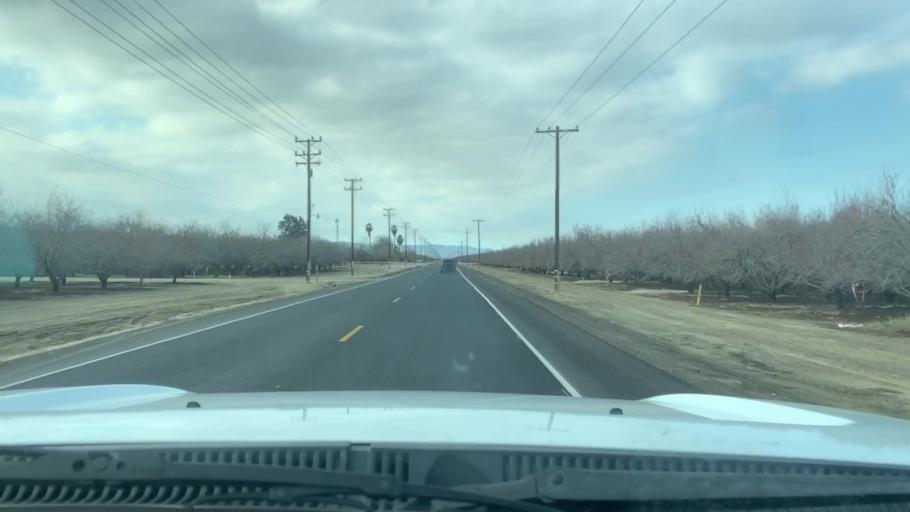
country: US
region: California
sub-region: Kern County
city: Lost Hills
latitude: 35.4993
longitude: -119.6667
